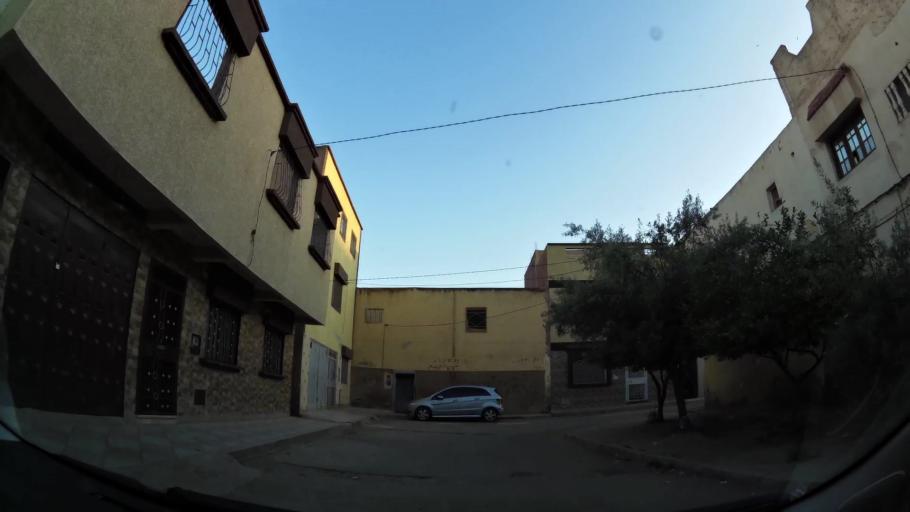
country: MA
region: Oriental
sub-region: Oujda-Angad
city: Oujda
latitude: 34.7021
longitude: -1.9113
